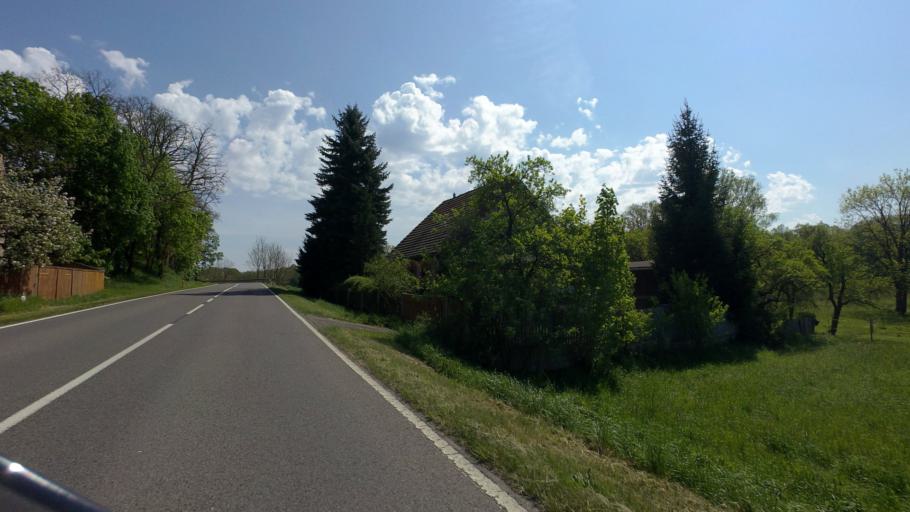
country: DE
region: Brandenburg
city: Lieberose
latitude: 51.9905
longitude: 14.3081
